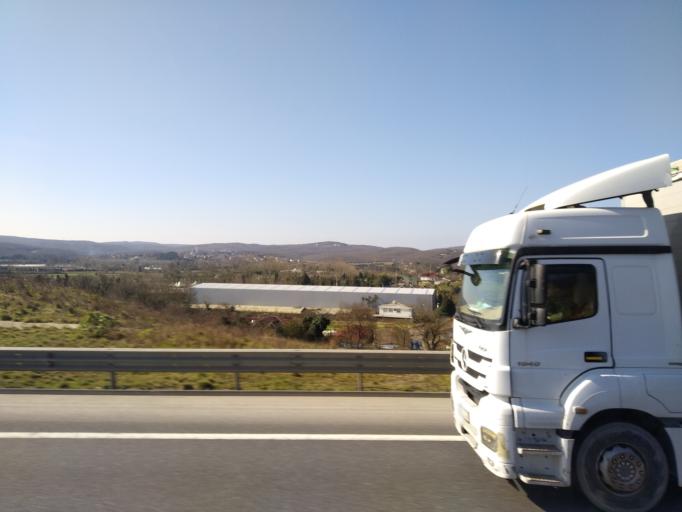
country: TR
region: Istanbul
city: Mahmut Sevket Pasa
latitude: 41.1320
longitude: 29.2865
